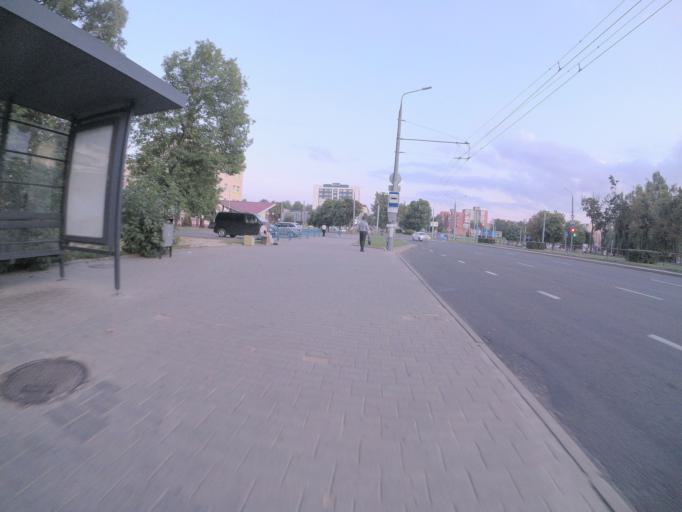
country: BY
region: Grodnenskaya
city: Hrodna
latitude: 53.7003
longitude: 23.8208
